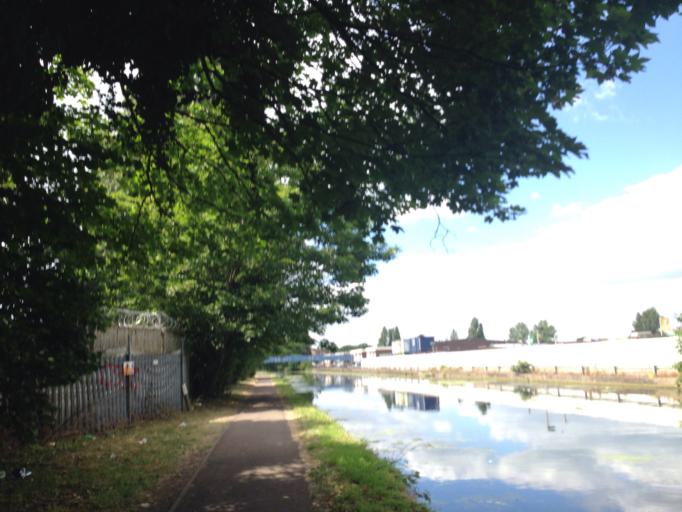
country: GB
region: England
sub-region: Greater London
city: Wembley
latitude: 51.5387
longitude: -0.2823
